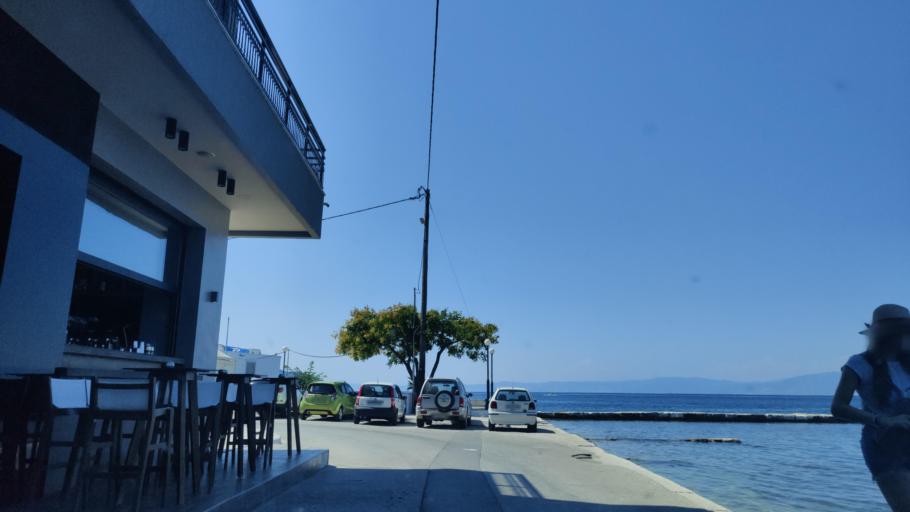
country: GR
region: East Macedonia and Thrace
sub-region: Nomos Kavalas
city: Thasos
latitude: 40.7807
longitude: 24.7109
